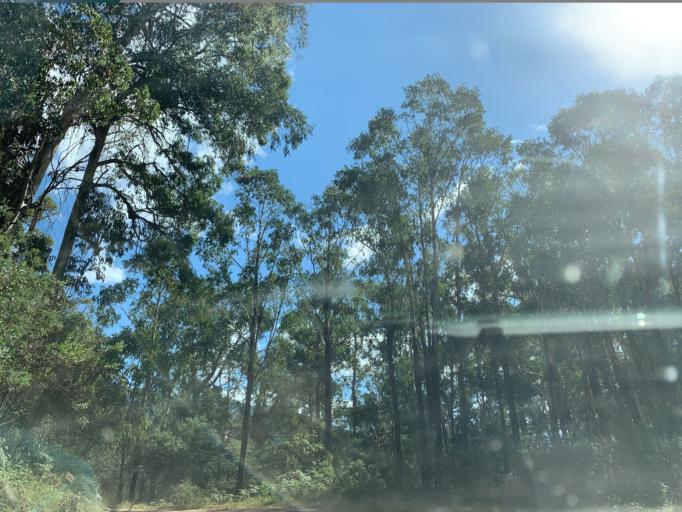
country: AU
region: Victoria
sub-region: Mansfield
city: Mansfield
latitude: -37.0965
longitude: 146.5133
